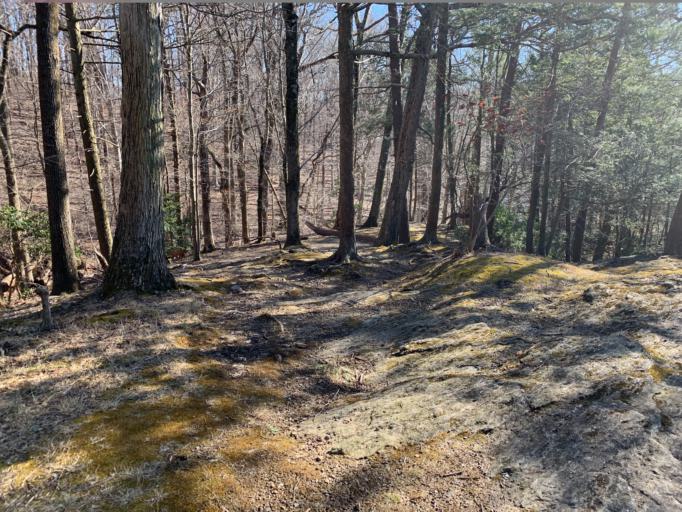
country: US
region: Pennsylvania
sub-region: Montgomery County
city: Rockledge
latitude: 40.0985
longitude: -75.0714
